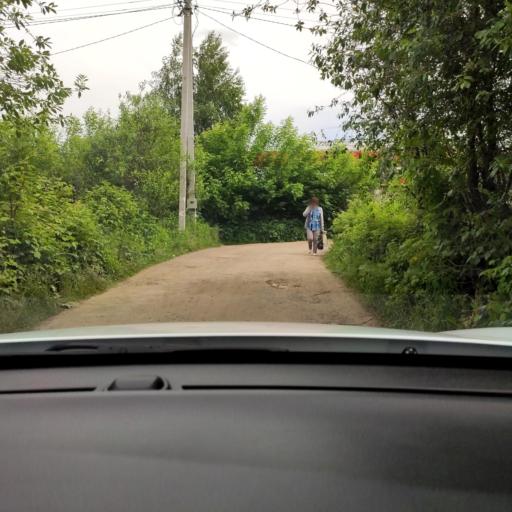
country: RU
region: Tatarstan
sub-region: Gorod Kazan'
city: Kazan
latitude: 55.8695
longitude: 49.1100
